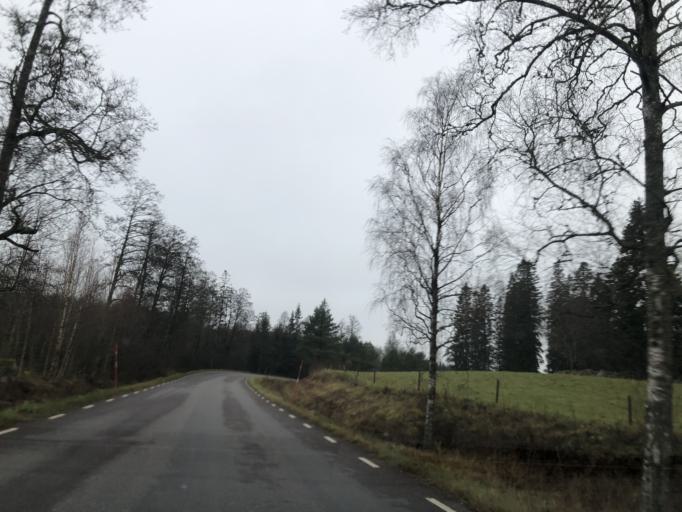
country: SE
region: Vaestra Goetaland
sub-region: Ulricehamns Kommun
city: Ulricehamn
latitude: 57.7619
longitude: 13.4768
